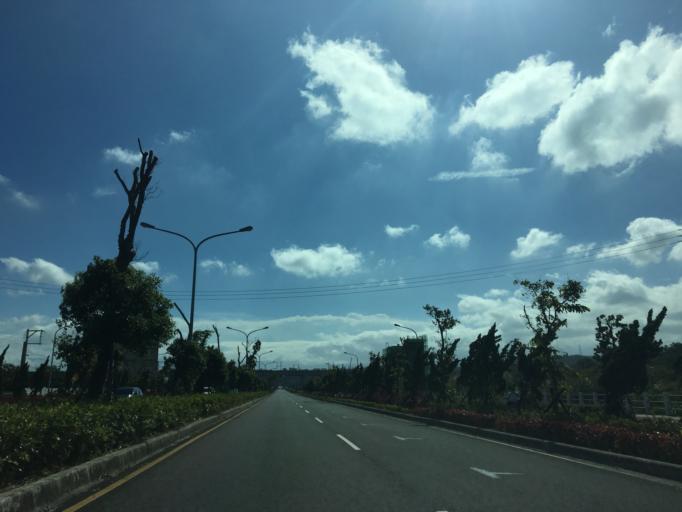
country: TW
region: Taiwan
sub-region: Hsinchu
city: Zhubei
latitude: 24.7882
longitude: 121.0297
